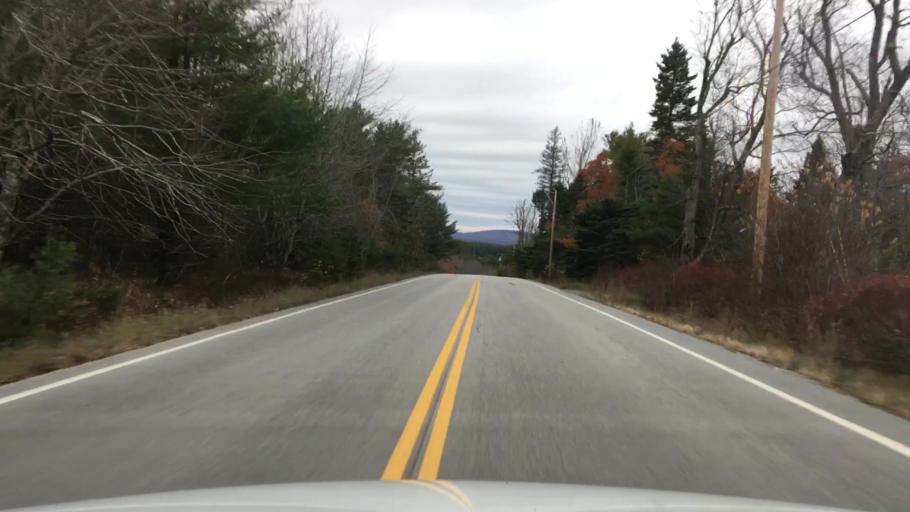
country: US
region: Maine
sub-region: Hancock County
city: Orland
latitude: 44.5348
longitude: -68.6779
